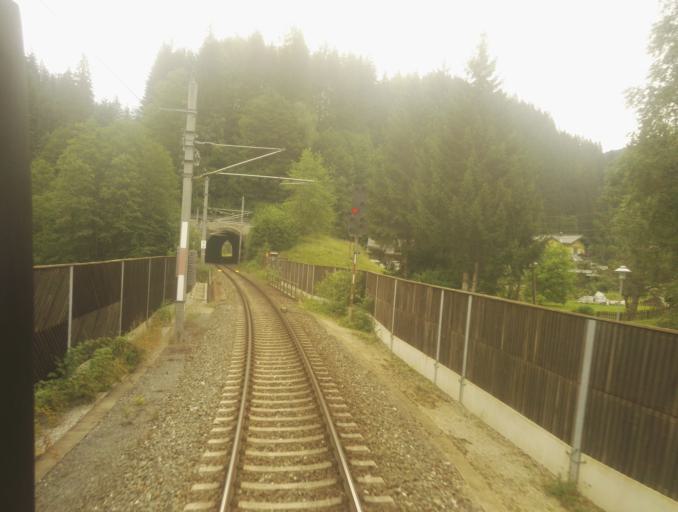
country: AT
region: Salzburg
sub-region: Politischer Bezirk Sankt Johann im Pongau
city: Huttau
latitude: 47.4137
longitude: 13.3113
